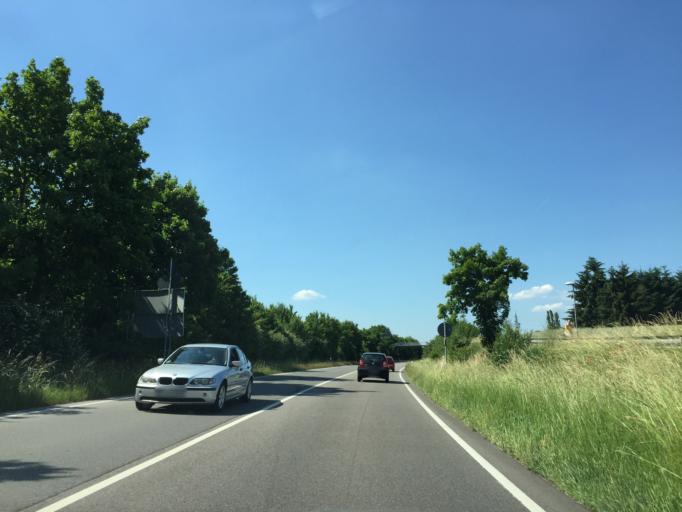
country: DE
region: Baden-Wuerttemberg
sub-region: Karlsruhe Region
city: Oftersheim
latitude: 49.3586
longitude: 8.5867
